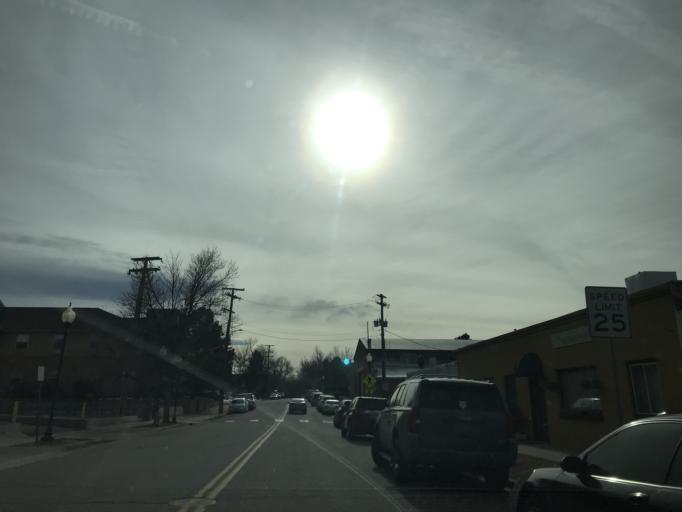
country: US
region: Colorado
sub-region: Arapahoe County
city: Littleton
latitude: 39.6124
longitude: -105.0184
